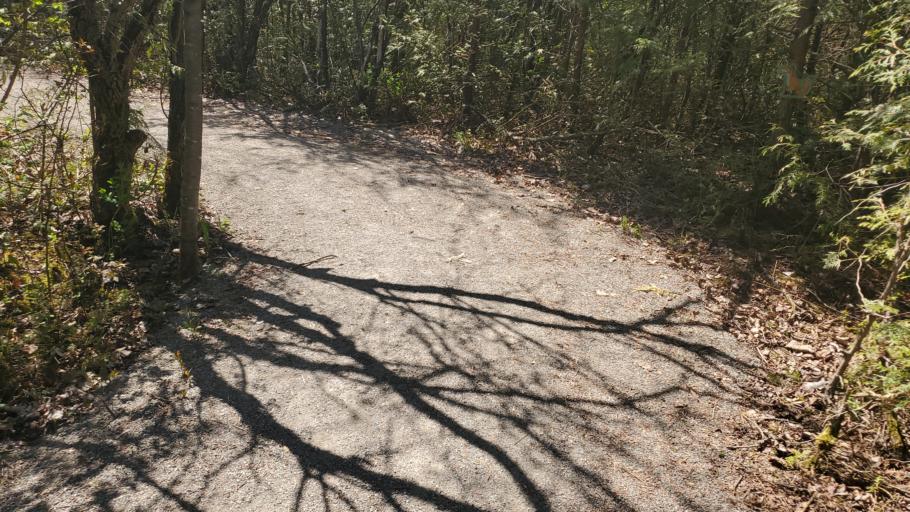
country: CA
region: Ontario
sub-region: Lanark County
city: Smiths Falls
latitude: 44.9141
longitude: -75.8300
